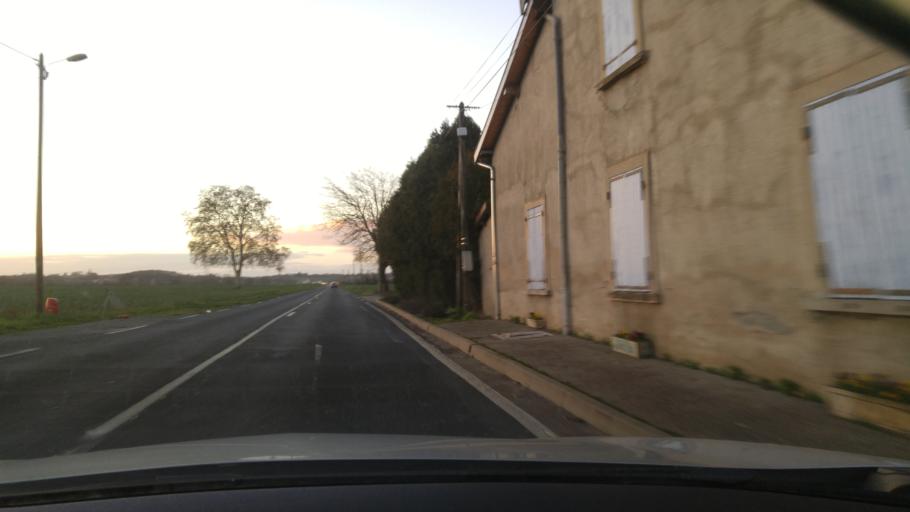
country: FR
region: Rhone-Alpes
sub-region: Departement de l'Isere
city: Satolas-et-Bonce
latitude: 45.7127
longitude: 5.1510
